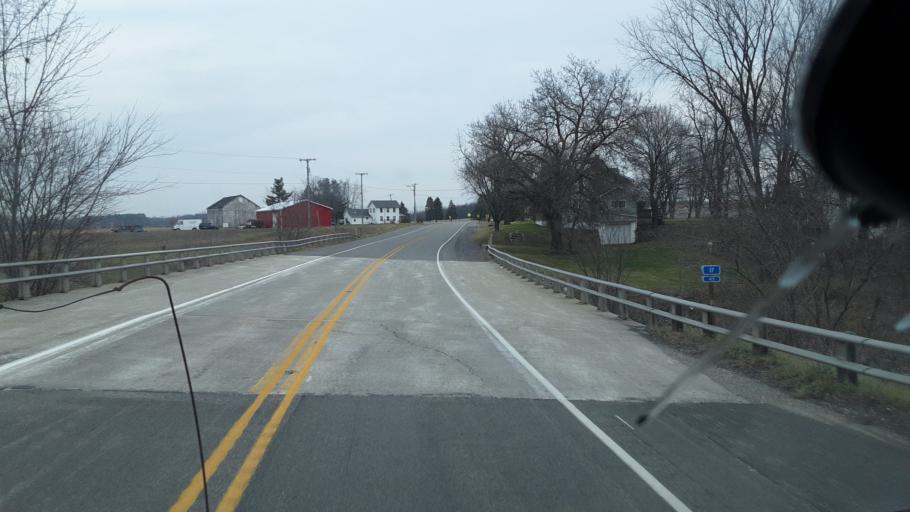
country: US
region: Indiana
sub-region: Noble County
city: Kendallville
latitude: 41.5555
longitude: -85.1701
